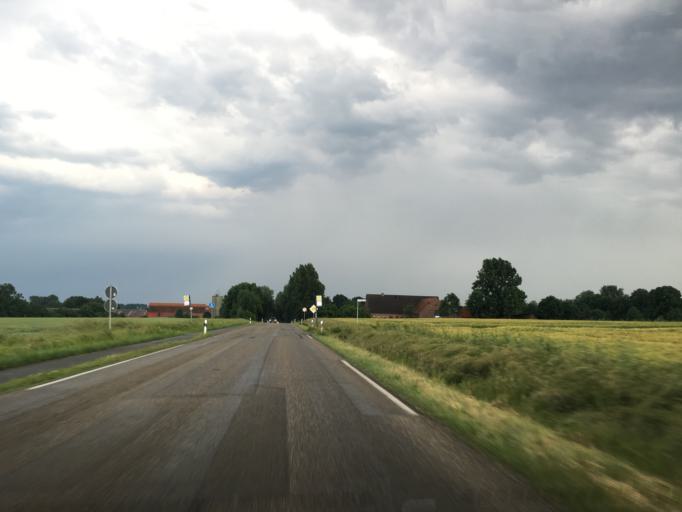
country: DE
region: North Rhine-Westphalia
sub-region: Regierungsbezirk Munster
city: Nordwalde
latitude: 52.0702
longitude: 7.4800
